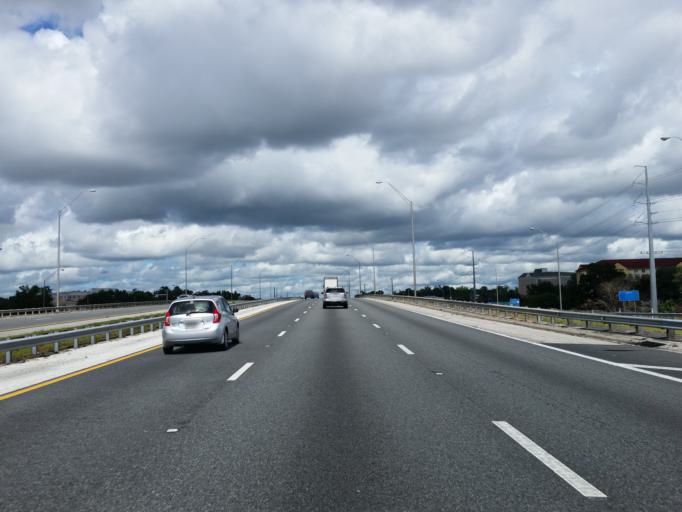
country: US
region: Florida
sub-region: Marion County
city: Ocala
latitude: 29.1471
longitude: -82.1850
